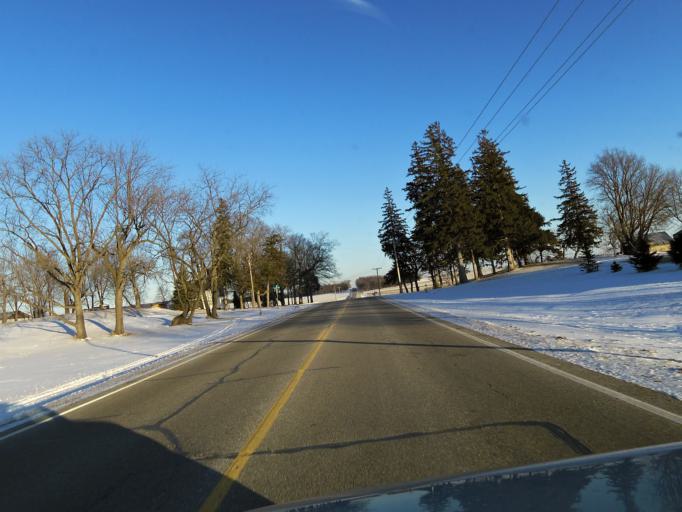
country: US
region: Minnesota
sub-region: Rice County
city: Northfield
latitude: 44.5438
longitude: -93.1885
